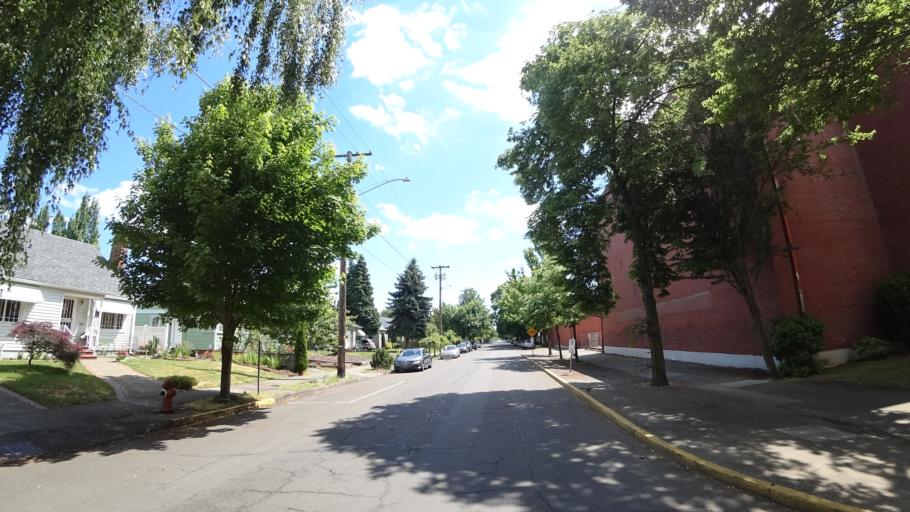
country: US
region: Oregon
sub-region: Multnomah County
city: Portland
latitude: 45.5605
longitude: -122.6712
